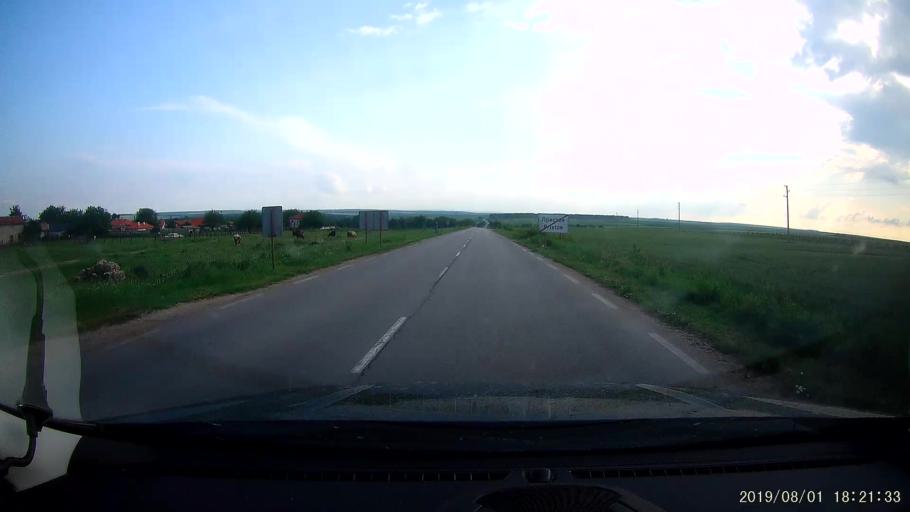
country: BG
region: Shumen
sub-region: Obshtina Kaolinovo
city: Kaolinovo
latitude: 43.6518
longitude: 27.0702
